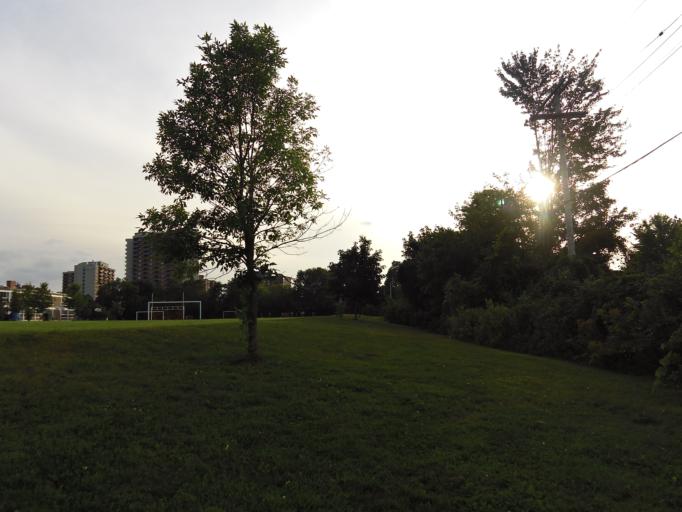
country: CA
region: Ontario
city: Bells Corners
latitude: 45.3453
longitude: -75.7844
